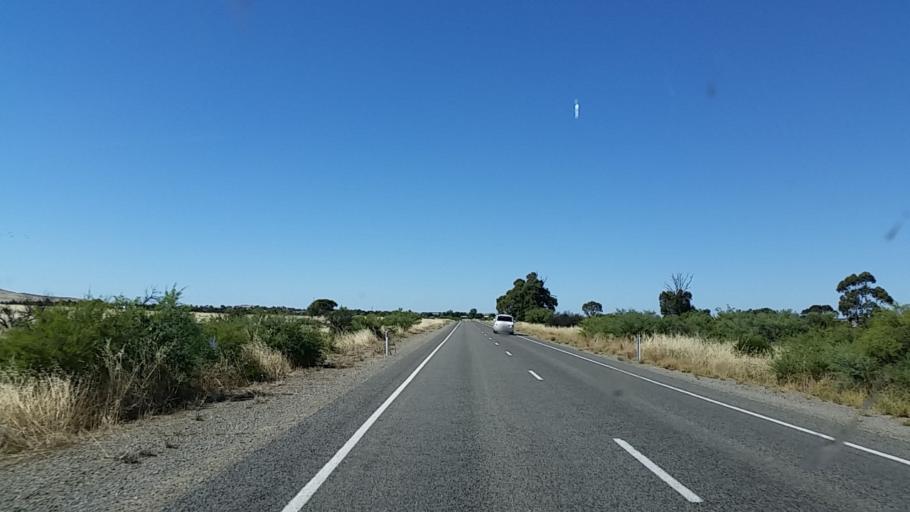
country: AU
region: South Australia
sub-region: Peterborough
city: Peterborough
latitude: -33.1644
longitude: 138.9158
